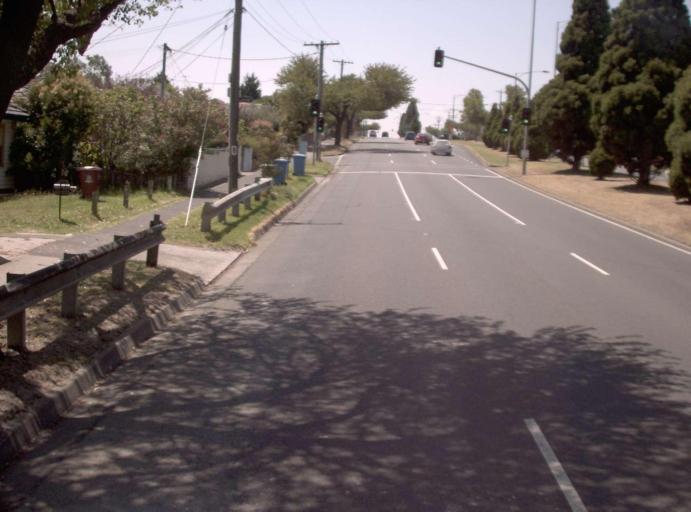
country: AU
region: Victoria
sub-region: Greater Dandenong
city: Springvale
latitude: -37.9391
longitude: 145.1545
